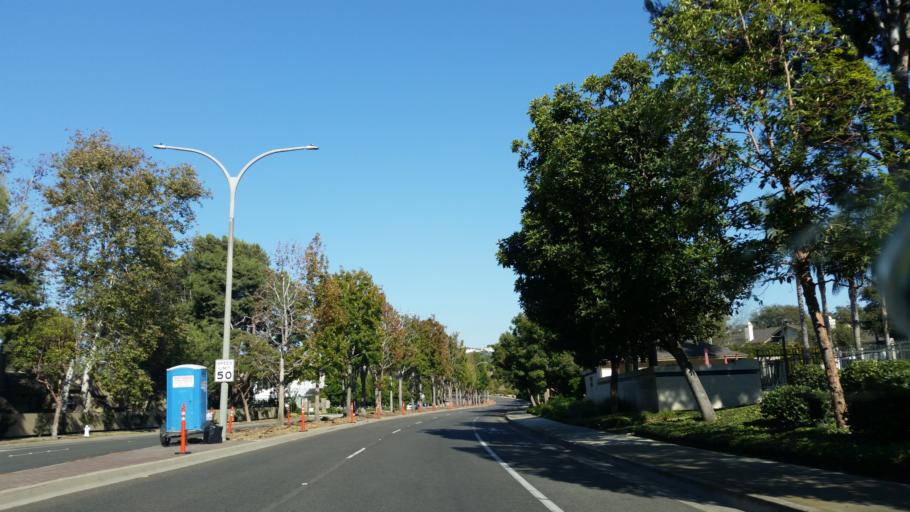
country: US
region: California
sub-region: Orange County
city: San Joaquin Hills
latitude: 33.6127
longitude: -117.8628
